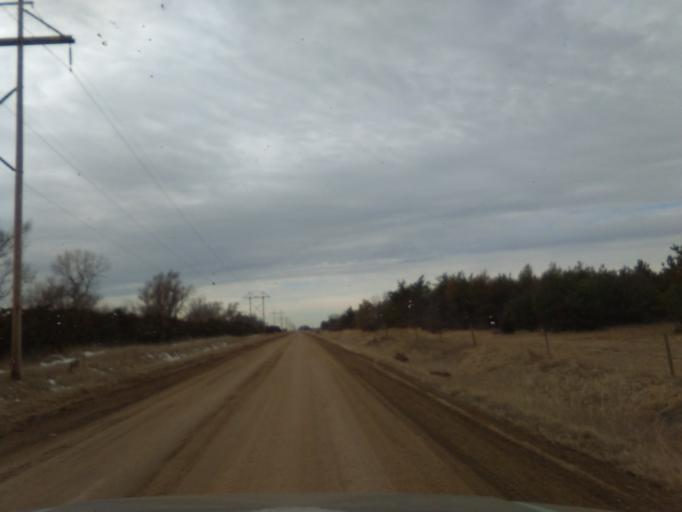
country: US
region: Nebraska
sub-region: Buffalo County
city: Gibbon
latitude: 40.6549
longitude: -98.7742
